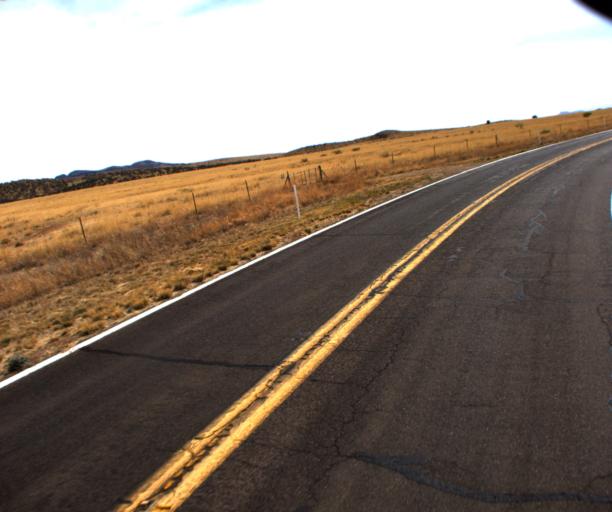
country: US
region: Arizona
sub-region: Cochise County
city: Willcox
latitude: 31.9929
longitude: -109.4404
